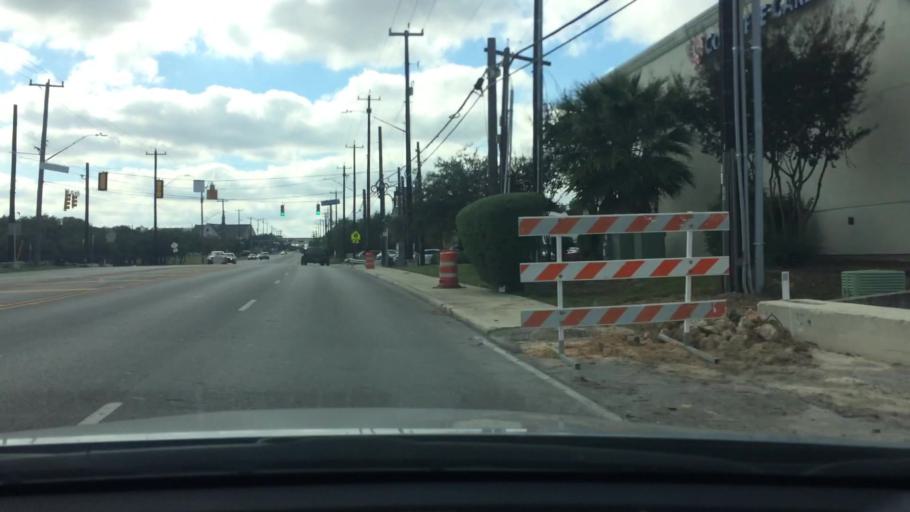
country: US
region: Texas
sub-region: Bexar County
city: Shavano Park
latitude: 29.5680
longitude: -98.5792
